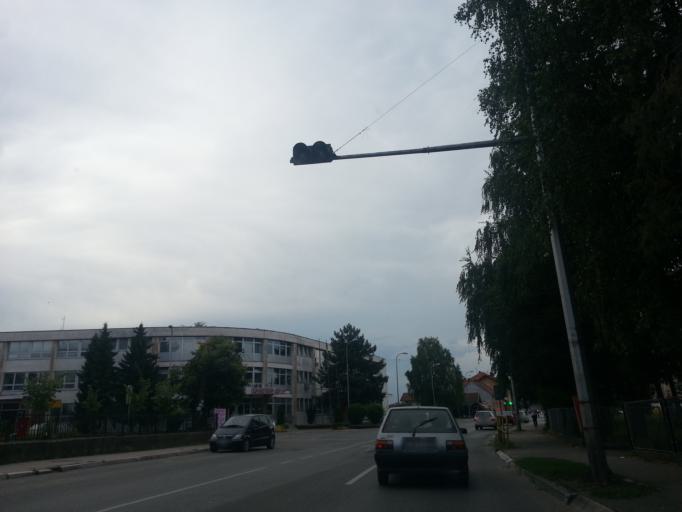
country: BA
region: Brcko
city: Brcko
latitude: 44.8779
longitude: 18.8003
